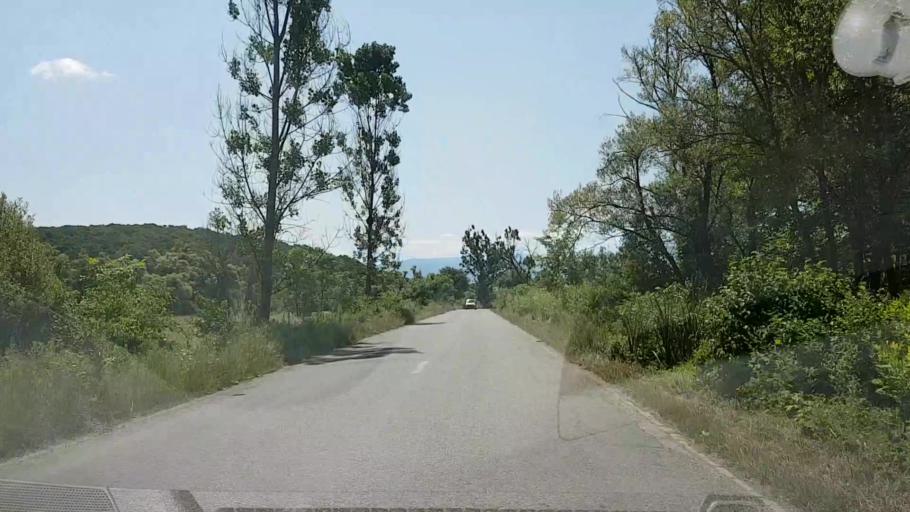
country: RO
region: Brasov
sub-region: Comuna Voila
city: Voila
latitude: 45.8540
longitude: 24.8308
